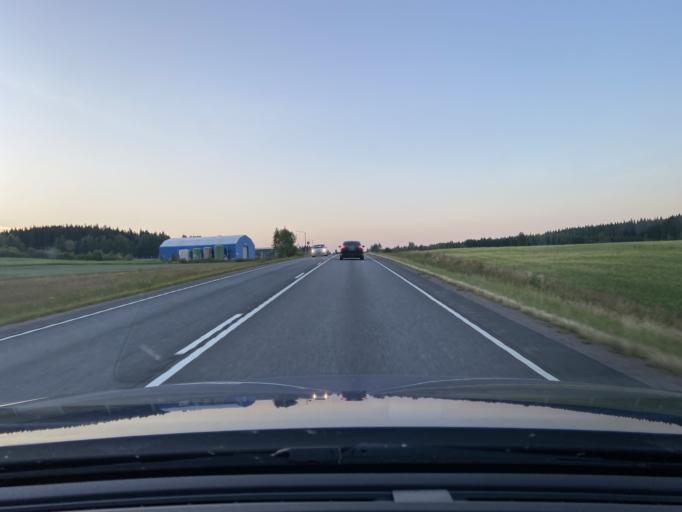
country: FI
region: Pirkanmaa
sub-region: Luoteis-Pirkanmaa
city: Ikaalinen
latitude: 61.8711
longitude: 22.9650
